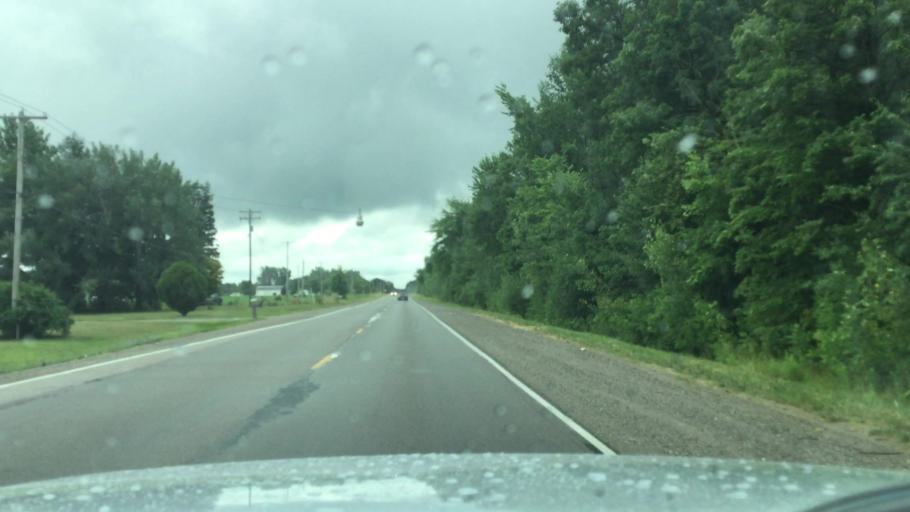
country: US
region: Michigan
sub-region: Genesee County
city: Flushing
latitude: 43.0745
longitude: -83.7732
